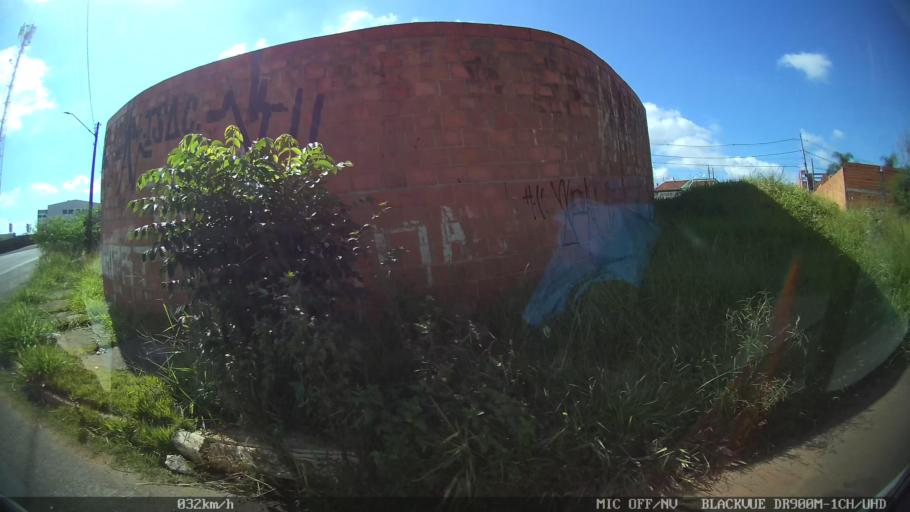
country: BR
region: Sao Paulo
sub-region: Hortolandia
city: Hortolandia
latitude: -22.8721
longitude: -47.2189
